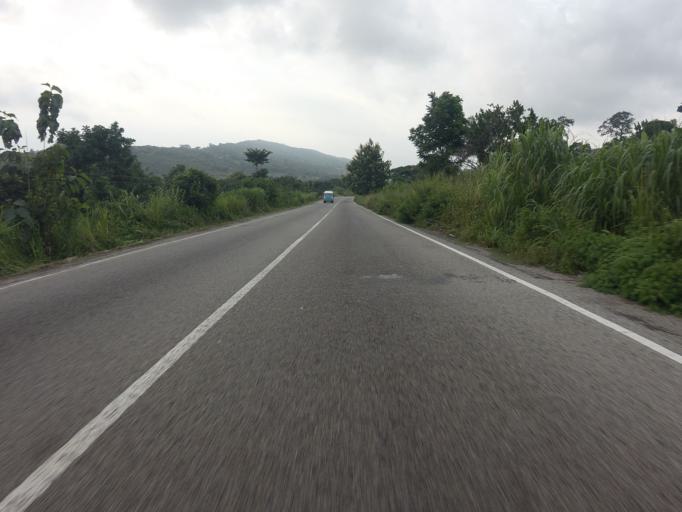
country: GH
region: Volta
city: Ho
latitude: 6.6389
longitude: 0.4673
